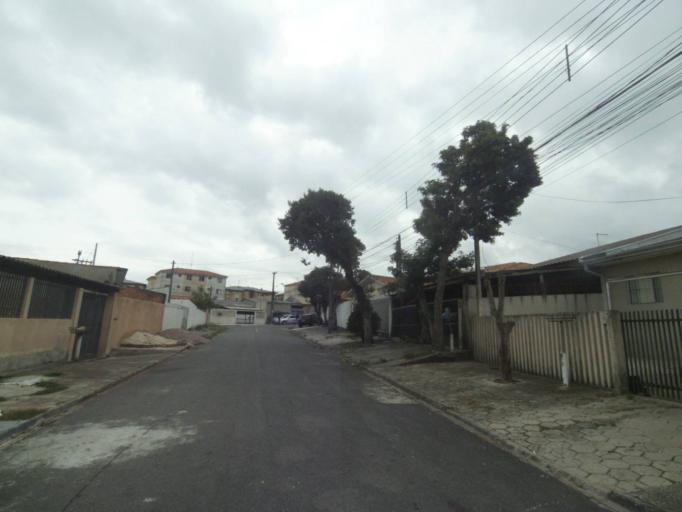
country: BR
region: Parana
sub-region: Sao Jose Dos Pinhais
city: Sao Jose dos Pinhais
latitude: -25.5470
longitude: -49.2651
